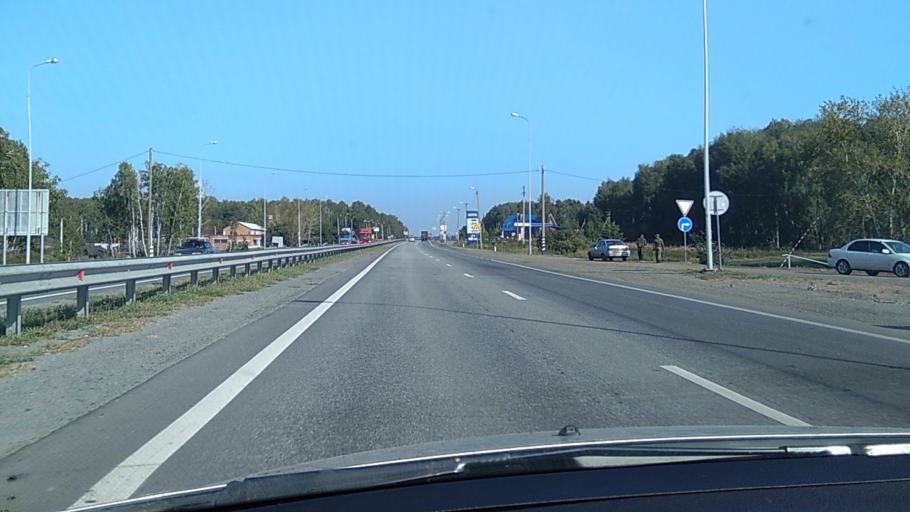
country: RU
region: Chelyabinsk
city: Sargazy
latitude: 55.0109
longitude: 61.2528
